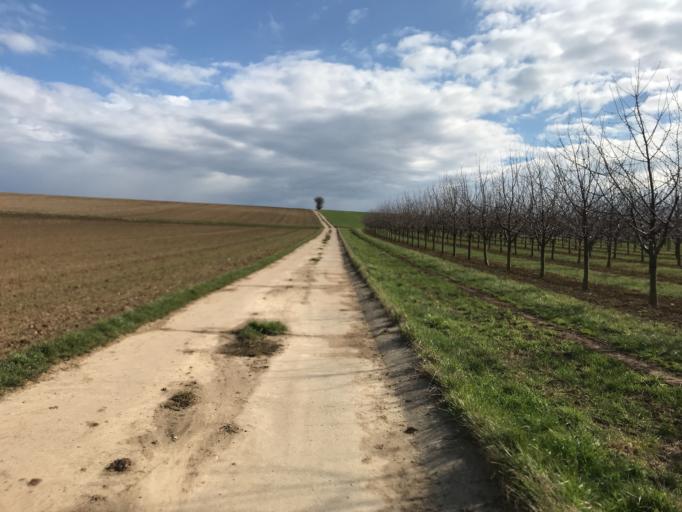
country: DE
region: Rheinland-Pfalz
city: Essenheim
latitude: 49.9068
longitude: 8.1714
